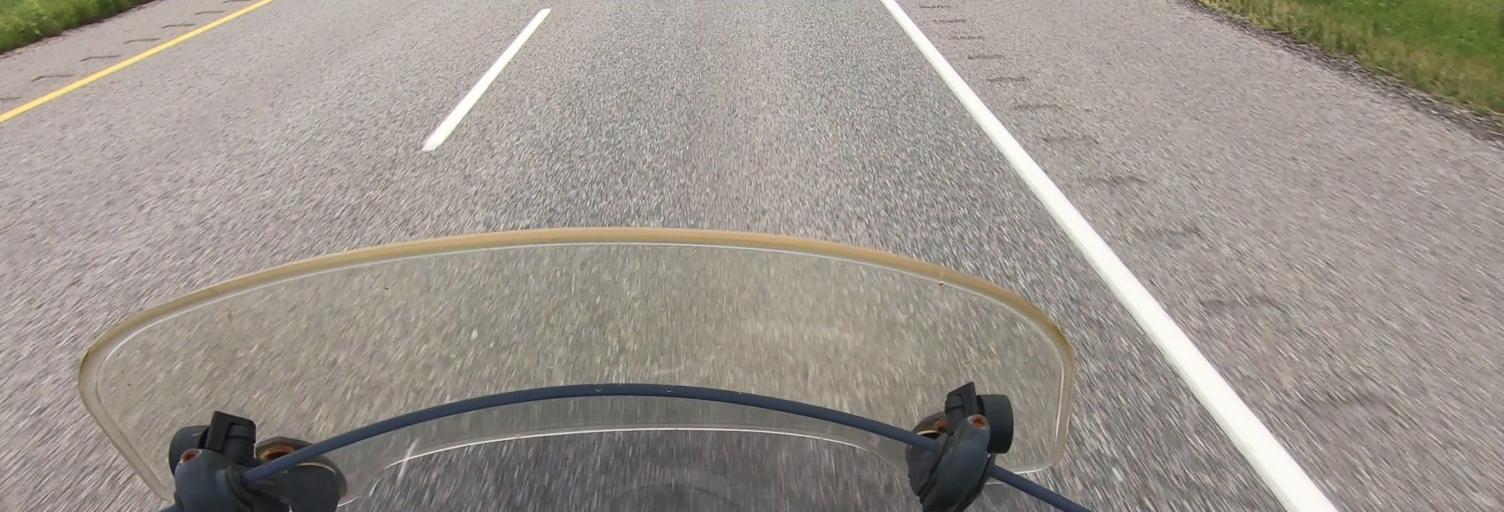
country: CA
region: Manitoba
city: Portage la Prairie
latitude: 49.9755
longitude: -98.6824
